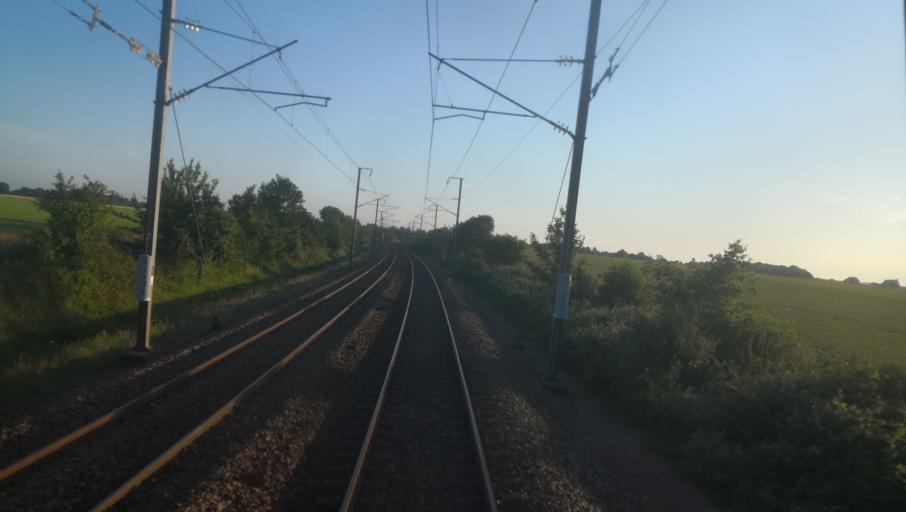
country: FR
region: Haute-Normandie
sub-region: Departement de l'Eure
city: Thiberville
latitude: 49.0727
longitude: 0.4511
